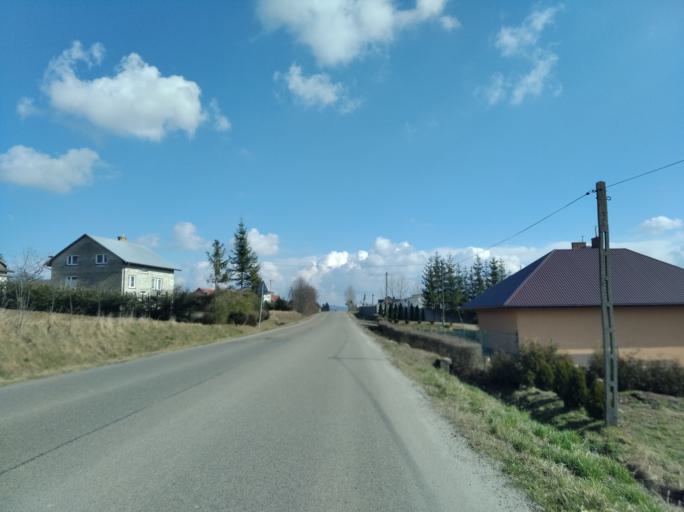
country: PL
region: Subcarpathian Voivodeship
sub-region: Powiat strzyzowski
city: Frysztak
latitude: 49.8494
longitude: 21.5356
